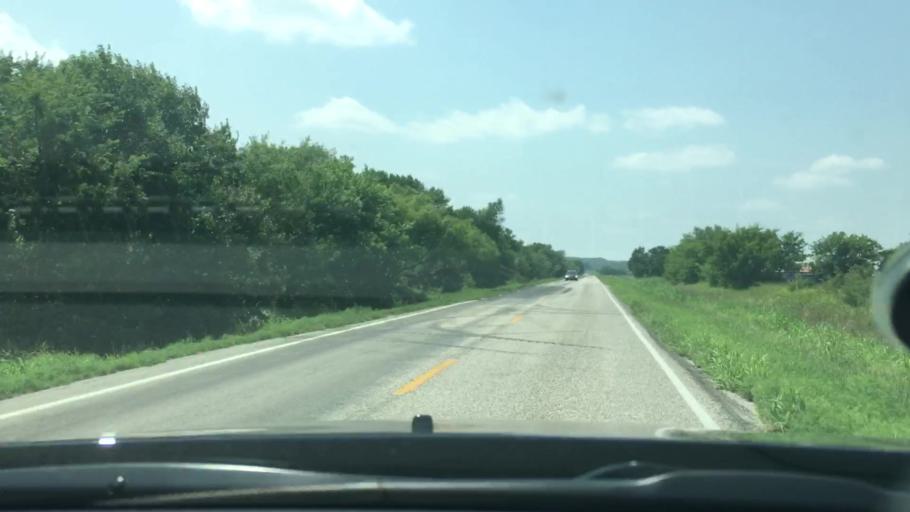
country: US
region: Oklahoma
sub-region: Johnston County
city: Tishomingo
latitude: 34.3761
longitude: -96.4764
